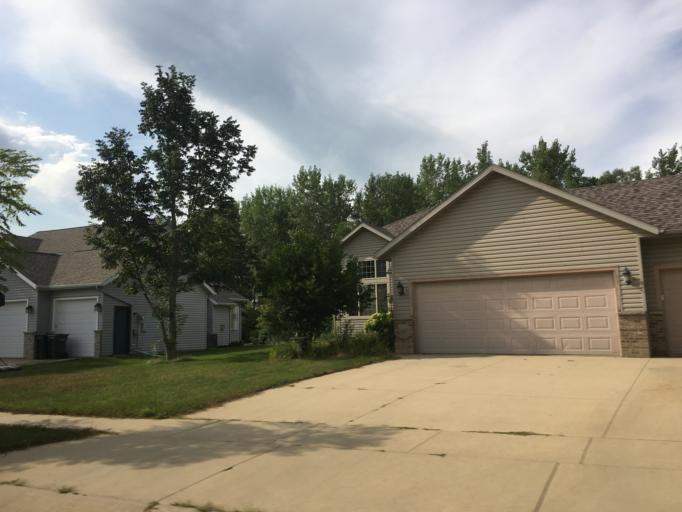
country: US
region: Minnesota
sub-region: Olmsted County
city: Oronoco
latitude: 44.0873
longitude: -92.5349
